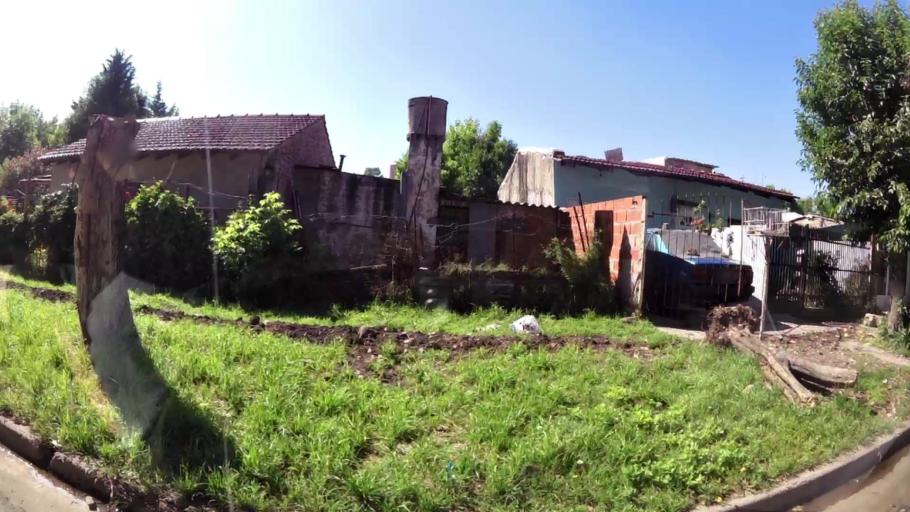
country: AR
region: Buenos Aires
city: Ituzaingo
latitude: -34.6212
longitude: -58.6604
